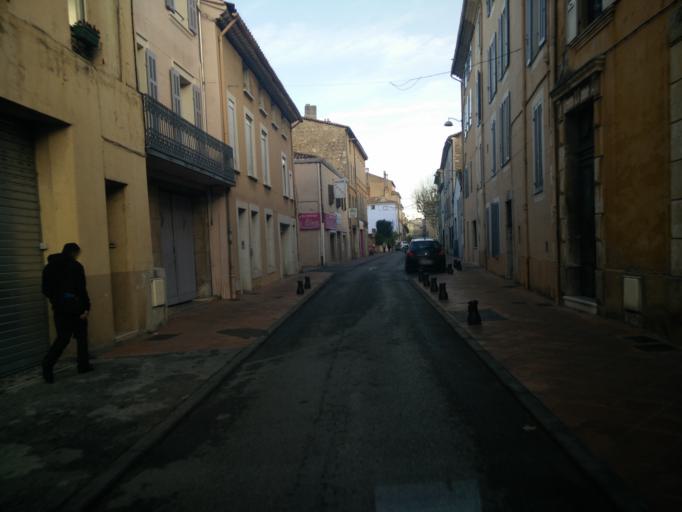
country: FR
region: Provence-Alpes-Cote d'Azur
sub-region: Departement du Var
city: Brignoles
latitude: 43.4071
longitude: 6.0570
